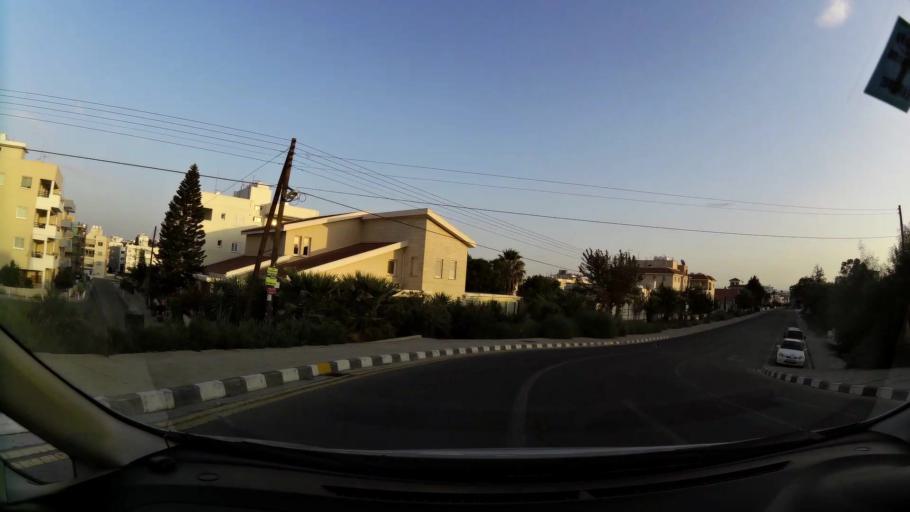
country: CY
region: Lefkosia
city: Nicosia
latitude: 35.1647
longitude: 33.3139
